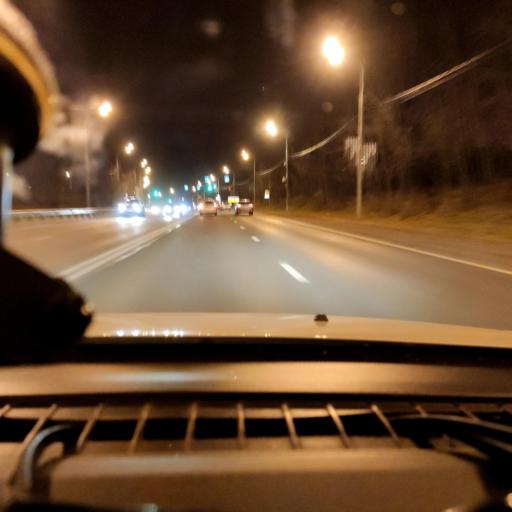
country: RU
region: Samara
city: Samara
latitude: 53.2935
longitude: 50.2246
